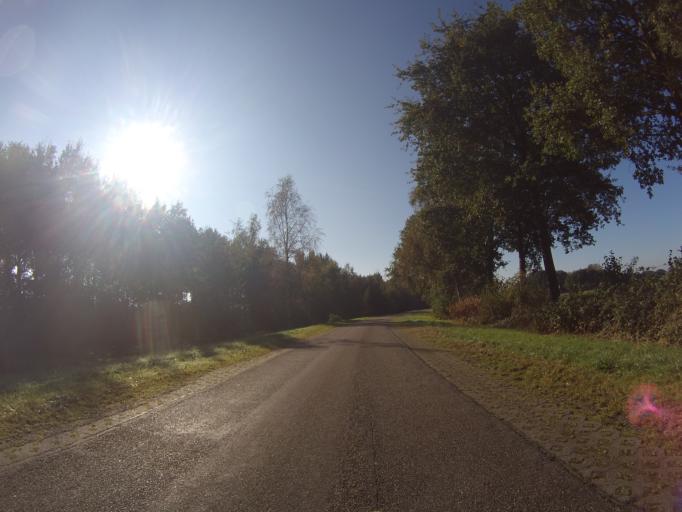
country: NL
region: Drenthe
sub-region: Gemeente Coevorden
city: Sleen
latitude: 52.7413
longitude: 6.7897
